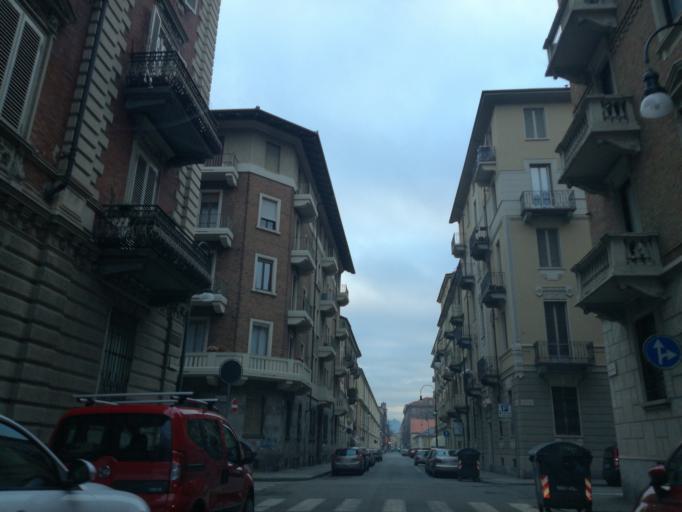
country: IT
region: Piedmont
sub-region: Provincia di Torino
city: Turin
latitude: 45.0778
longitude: 7.6721
